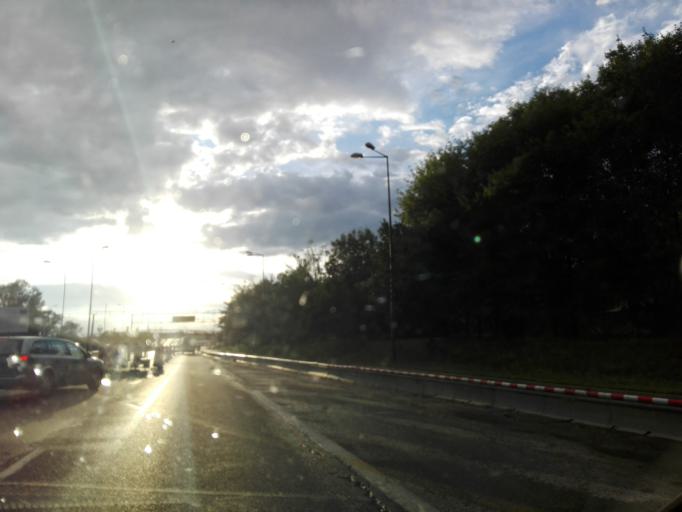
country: PL
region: Lublin Voivodeship
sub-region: Powiat lubelski
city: Lublin
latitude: 51.2565
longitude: 22.5399
